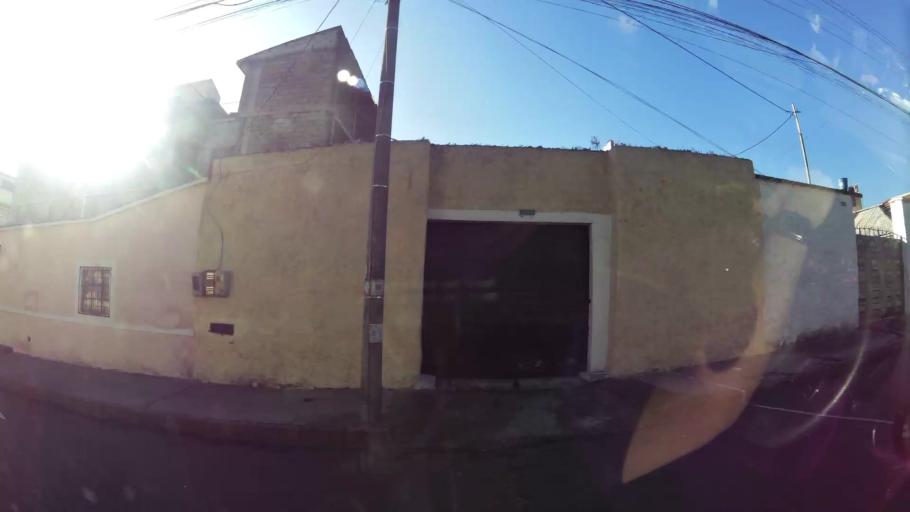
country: EC
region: Pichincha
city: Quito
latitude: -0.2430
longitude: -78.5152
